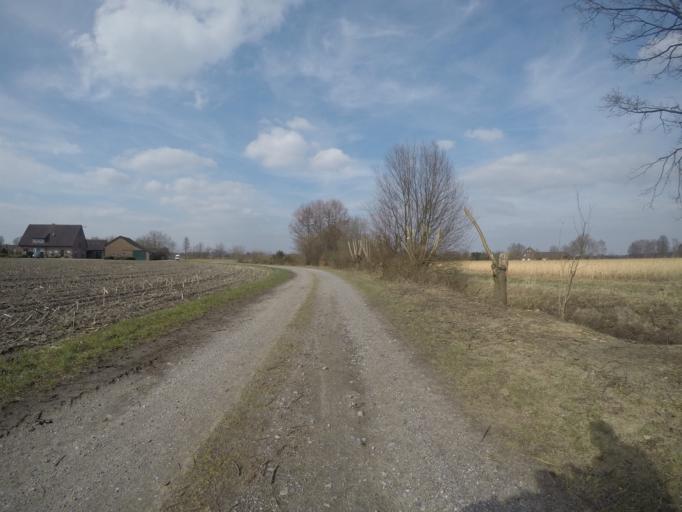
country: DE
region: North Rhine-Westphalia
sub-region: Regierungsbezirk Munster
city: Rhede
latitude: 51.7918
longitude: 6.7187
